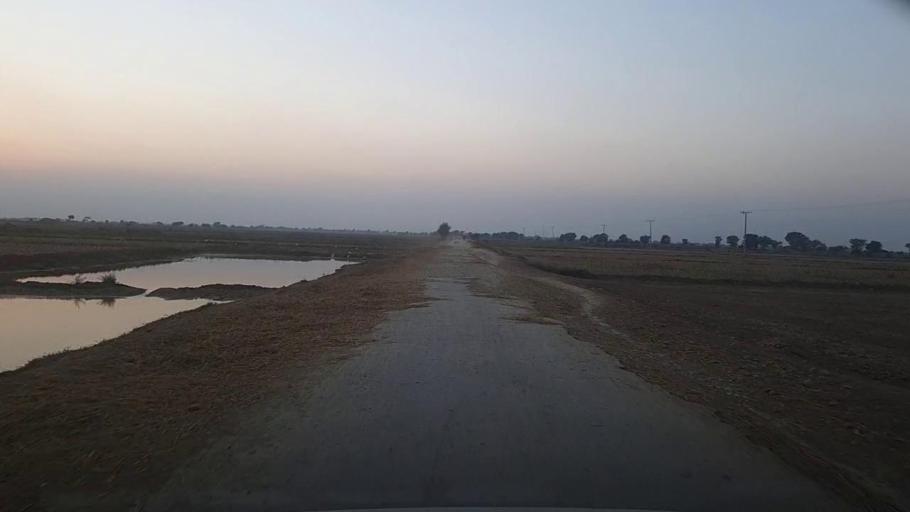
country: PK
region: Sindh
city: Khairpur Nathan Shah
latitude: 27.1801
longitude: 67.6139
